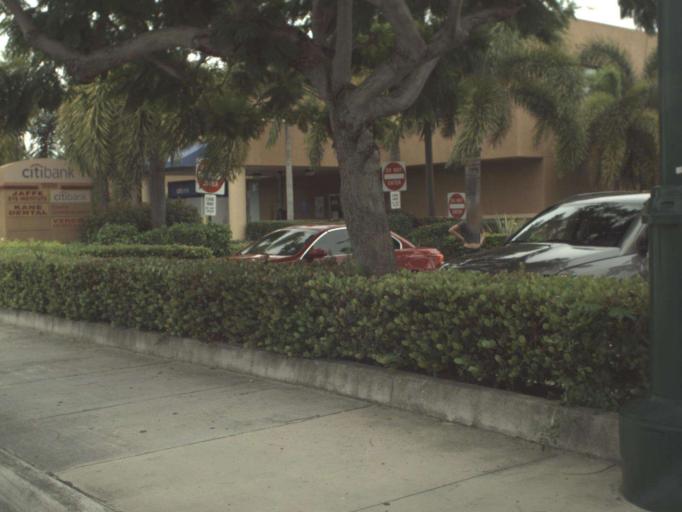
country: US
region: Florida
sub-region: Miami-Dade County
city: Ojus
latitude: 25.9501
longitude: -80.1465
